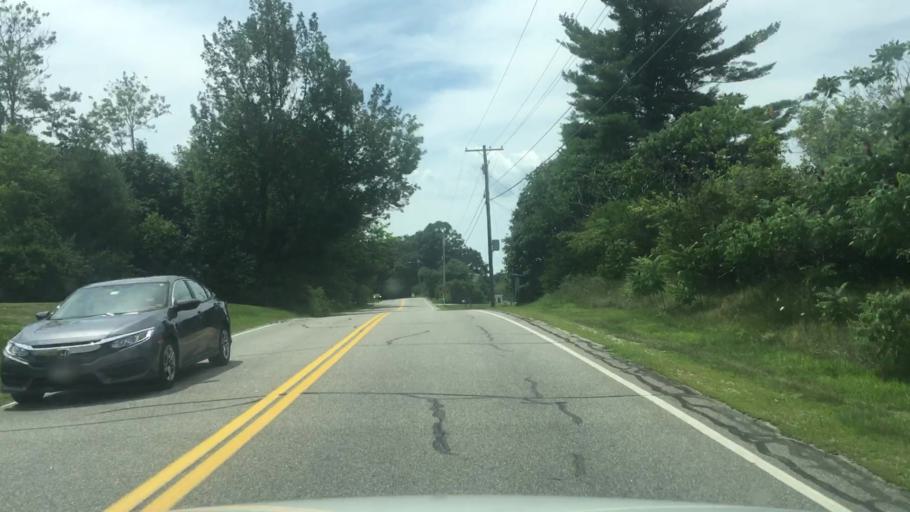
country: US
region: Maine
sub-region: Cumberland County
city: Scarborough
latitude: 43.5811
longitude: -70.2652
